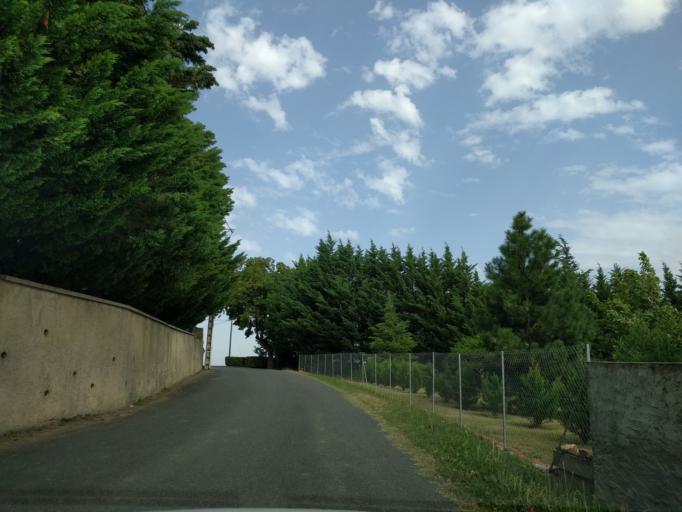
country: FR
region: Midi-Pyrenees
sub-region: Departement du Tarn
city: Saix
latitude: 43.6508
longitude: 2.1971
